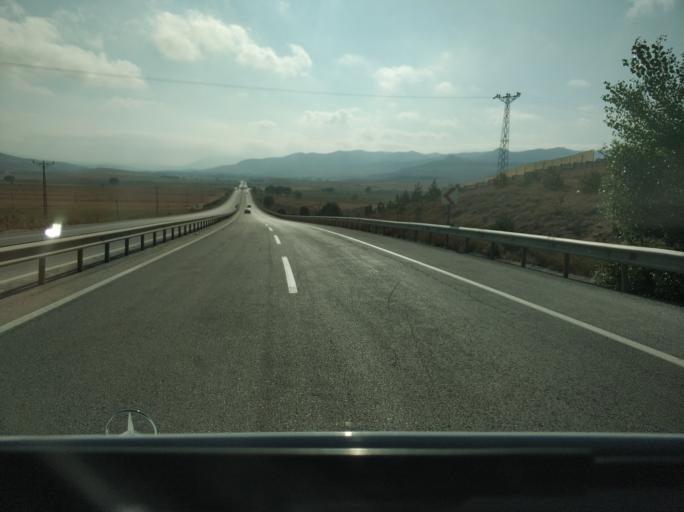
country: TR
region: Sivas
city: Yildizeli
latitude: 39.8345
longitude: 36.4161
